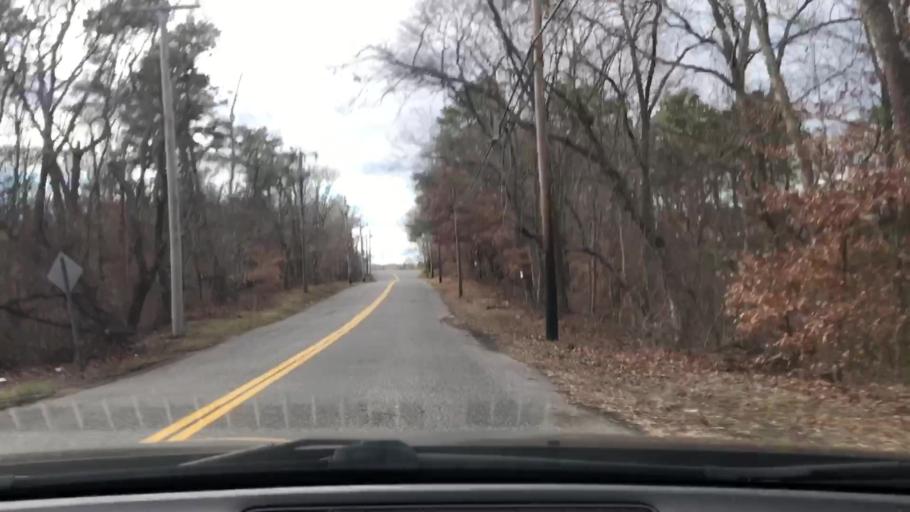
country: US
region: New York
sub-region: Suffolk County
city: Baiting Hollow
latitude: 40.9344
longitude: -72.7067
